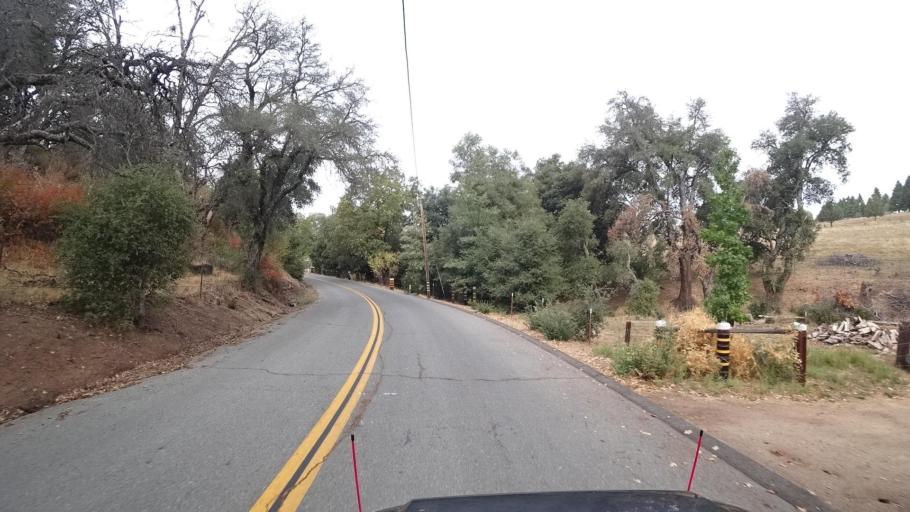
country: US
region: California
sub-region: San Diego County
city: Julian
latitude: 33.0458
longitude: -116.6104
